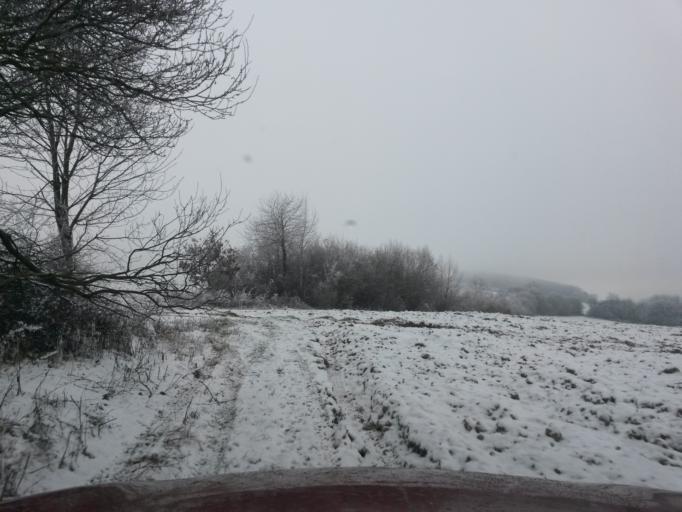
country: SK
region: Presovsky
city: Sabinov
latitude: 48.9806
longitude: 21.0835
